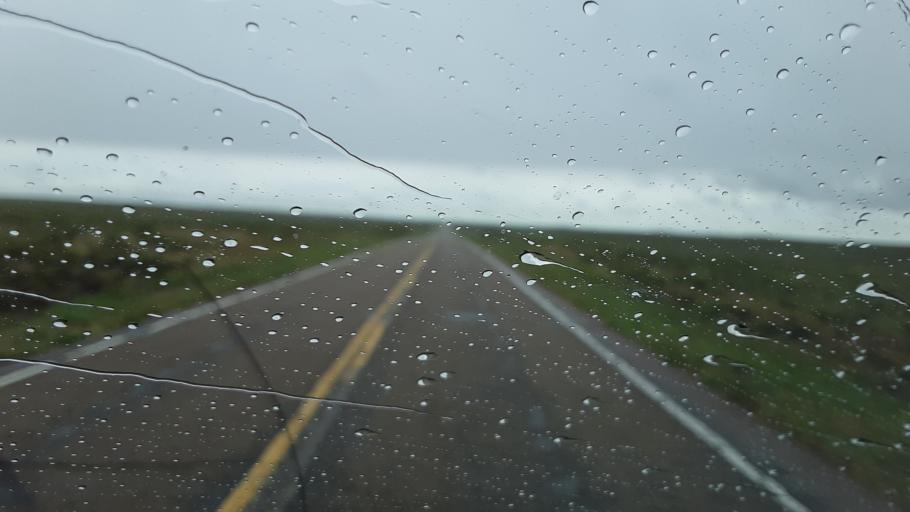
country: US
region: Colorado
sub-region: Lincoln County
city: Hugo
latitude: 38.8495
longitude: -103.2190
